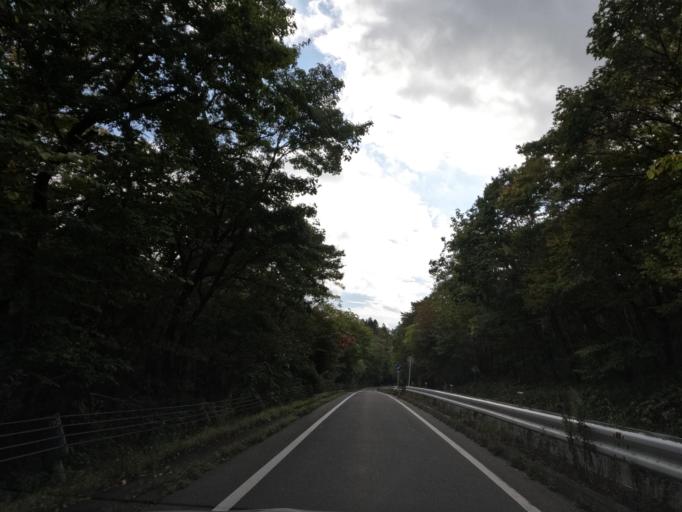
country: JP
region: Hokkaido
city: Chitose
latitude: 42.8064
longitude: 141.5849
